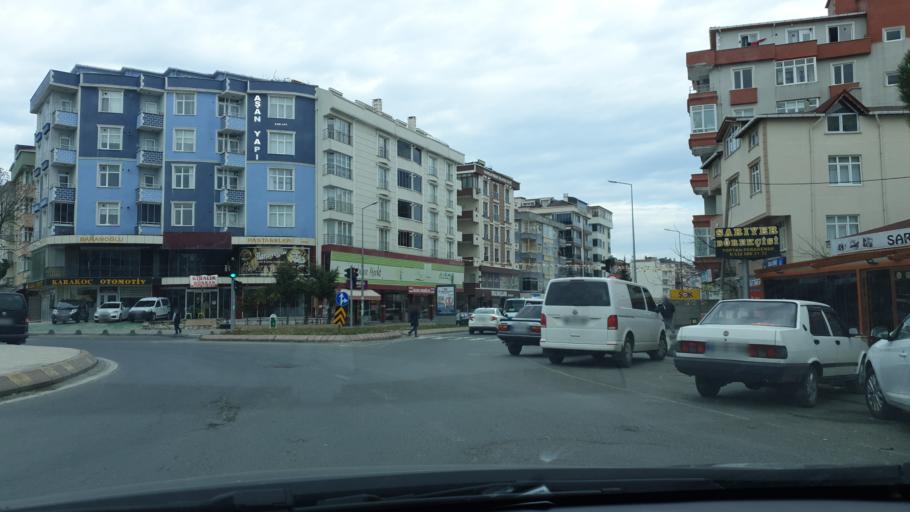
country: TR
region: Tekirdag
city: Cerkezkoey
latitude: 41.2878
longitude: 27.9905
